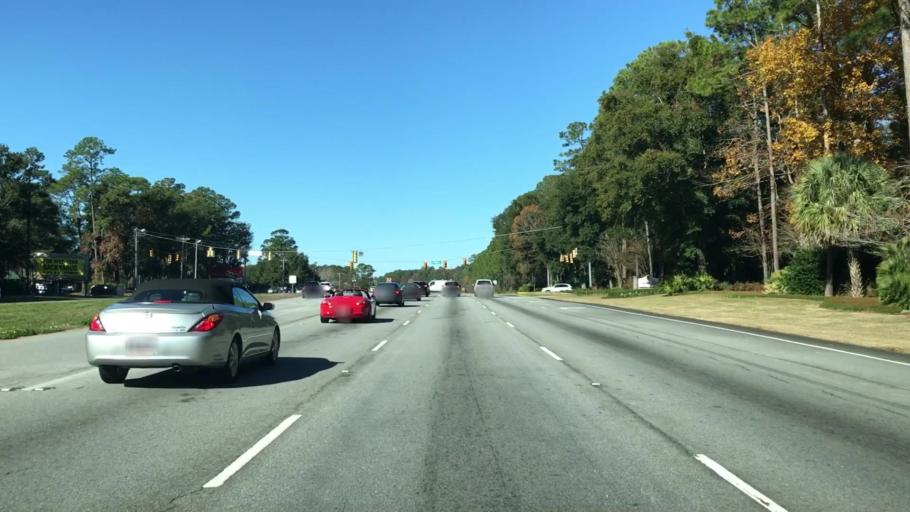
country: US
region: South Carolina
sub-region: Beaufort County
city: Bluffton
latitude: 32.2434
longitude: -80.8251
